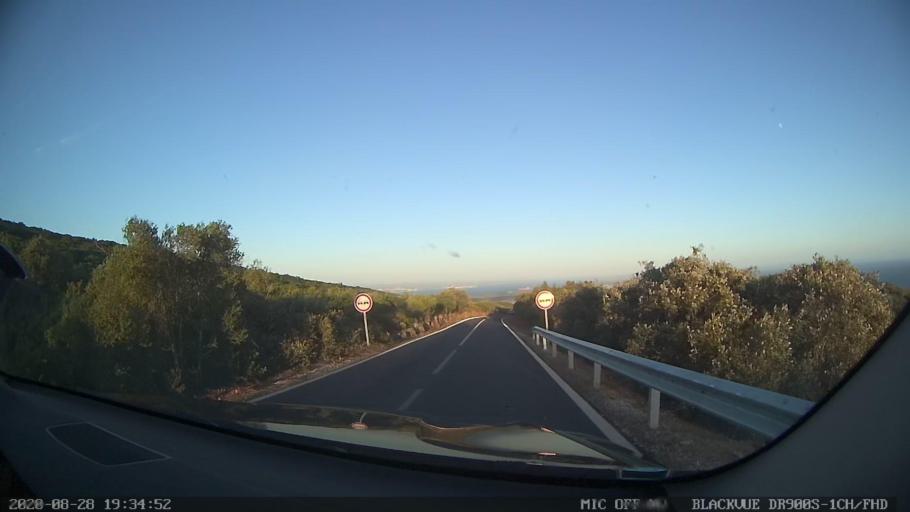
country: PT
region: Setubal
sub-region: Setubal
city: Setubal
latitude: 38.4893
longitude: -8.9522
